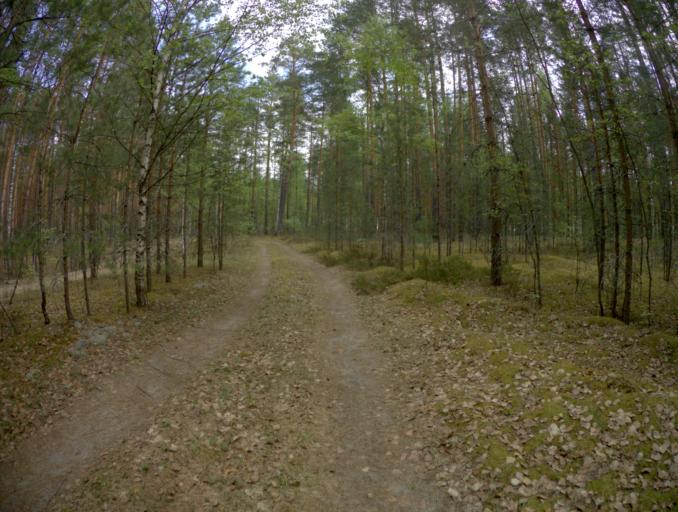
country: RU
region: Ivanovo
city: Talitsy
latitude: 56.4862
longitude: 42.1670
